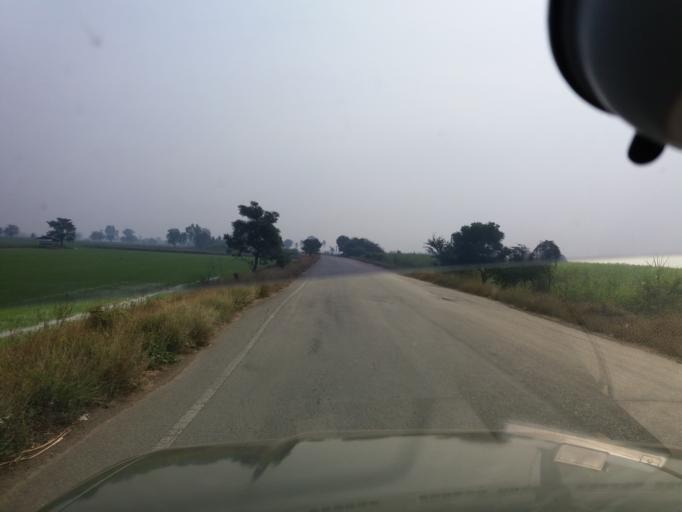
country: TH
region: Suphan Buri
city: Doem Bang Nang Buat
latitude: 14.8529
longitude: 100.1330
